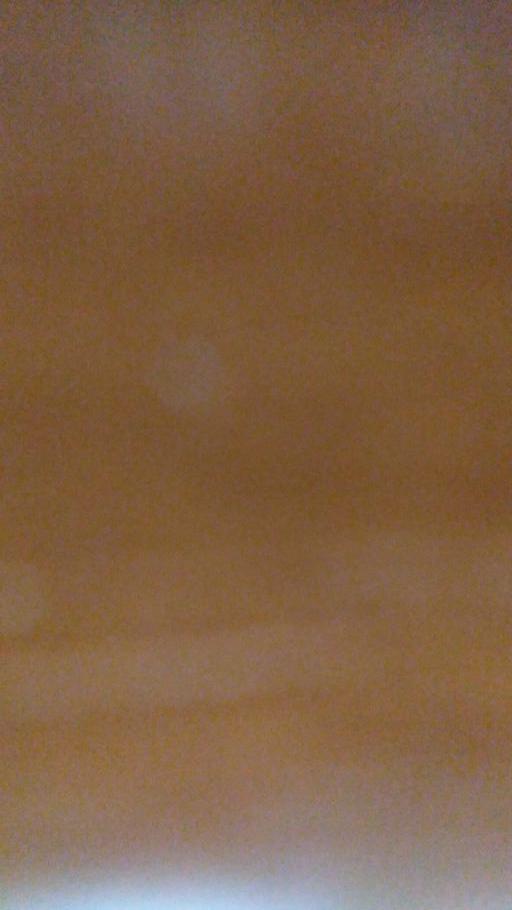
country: RU
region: Tula
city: Volovo
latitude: 53.5076
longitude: 38.1140
